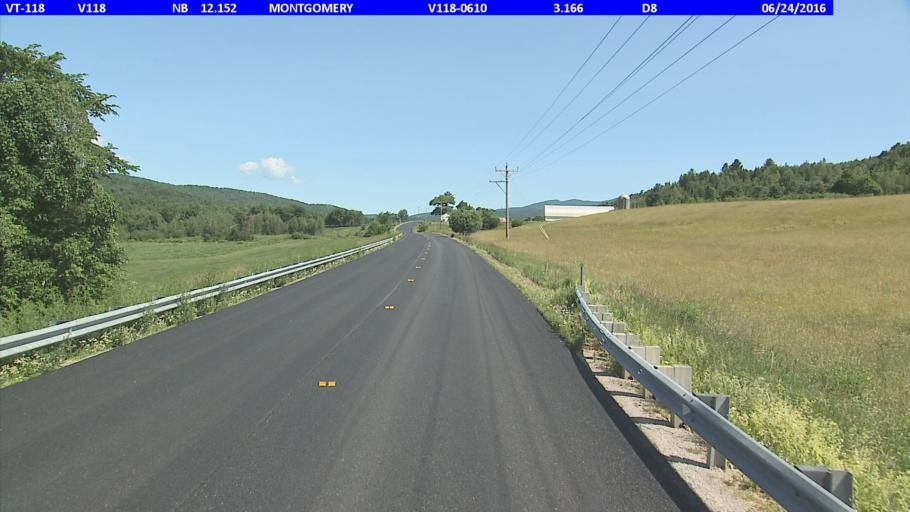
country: US
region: Vermont
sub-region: Franklin County
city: Richford
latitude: 44.8434
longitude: -72.6097
